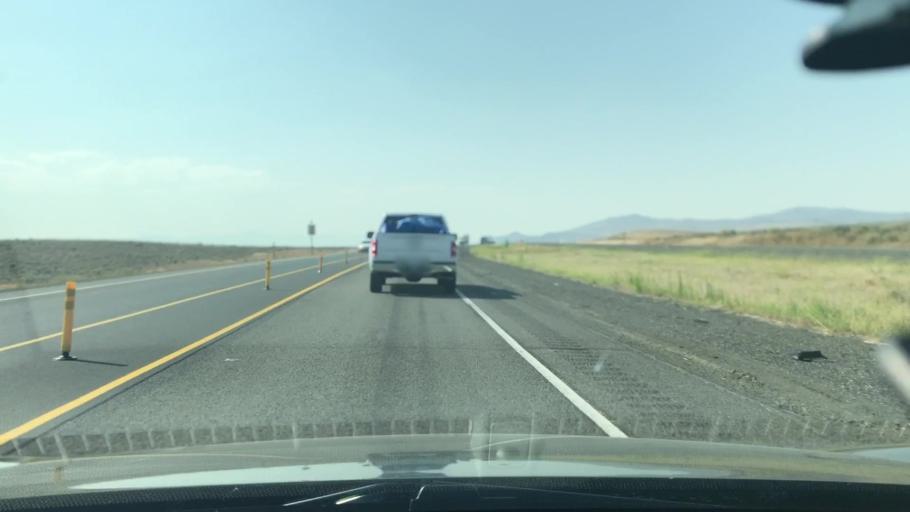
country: US
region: Oregon
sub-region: Baker County
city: Baker City
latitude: 44.6893
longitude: -117.6829
